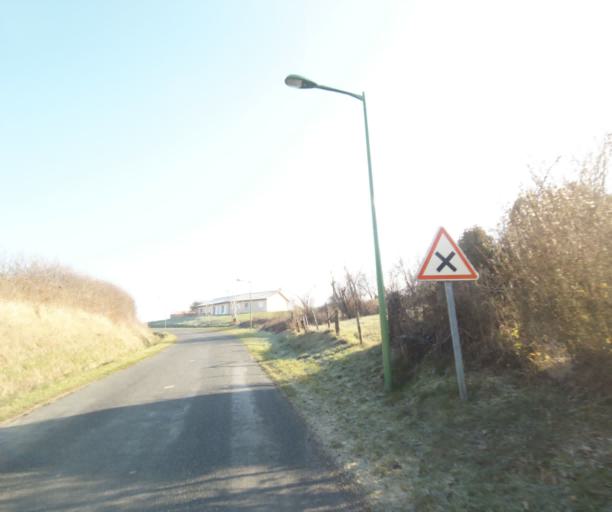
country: FR
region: Champagne-Ardenne
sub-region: Departement de la Haute-Marne
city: Chevillon
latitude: 48.4923
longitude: 5.0712
